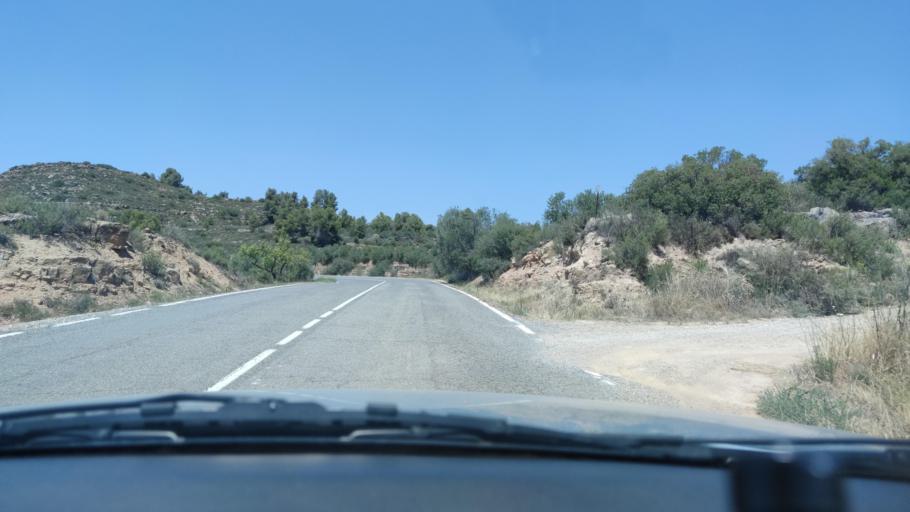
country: ES
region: Catalonia
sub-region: Provincia de Lleida
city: el Cogul
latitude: 41.4277
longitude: 0.6648
